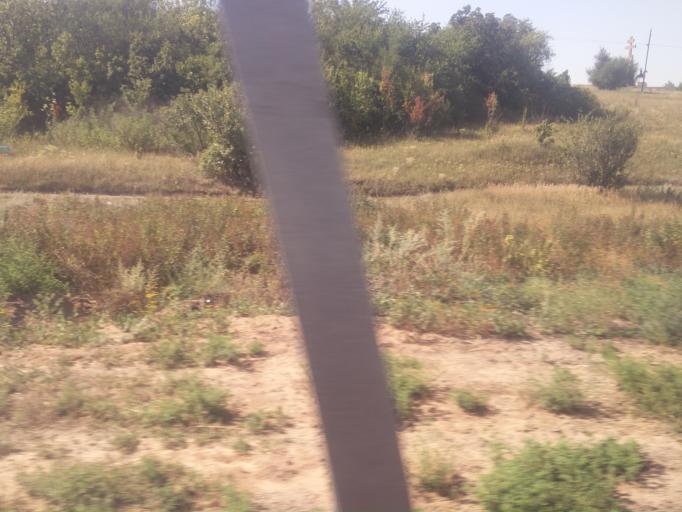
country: RU
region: Rostov
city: Krasnyy Sulin
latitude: 47.8757
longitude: 40.1170
